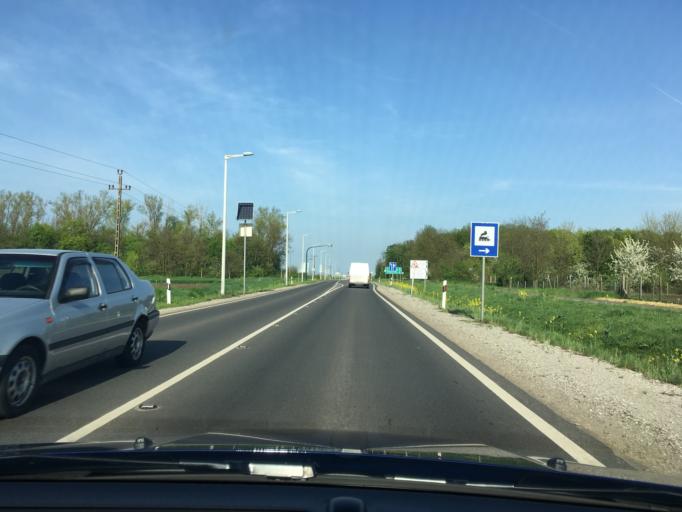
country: HU
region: Bekes
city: Ujkigyos
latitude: 46.6622
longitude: 20.9517
